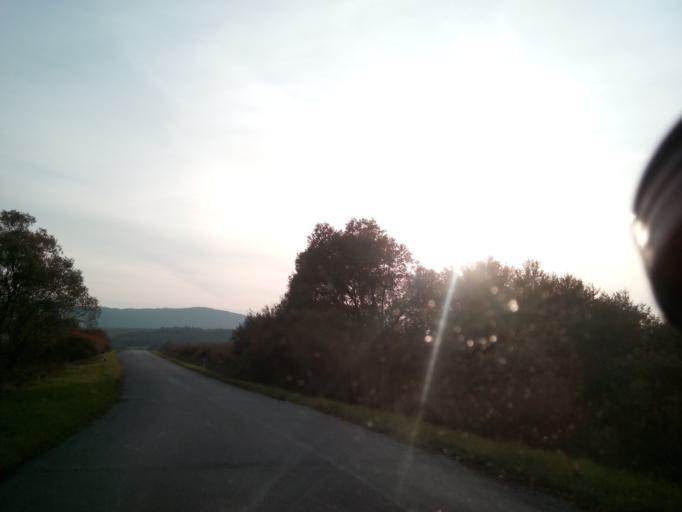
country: SK
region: Presovsky
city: Svidnik
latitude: 49.3749
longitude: 21.4762
